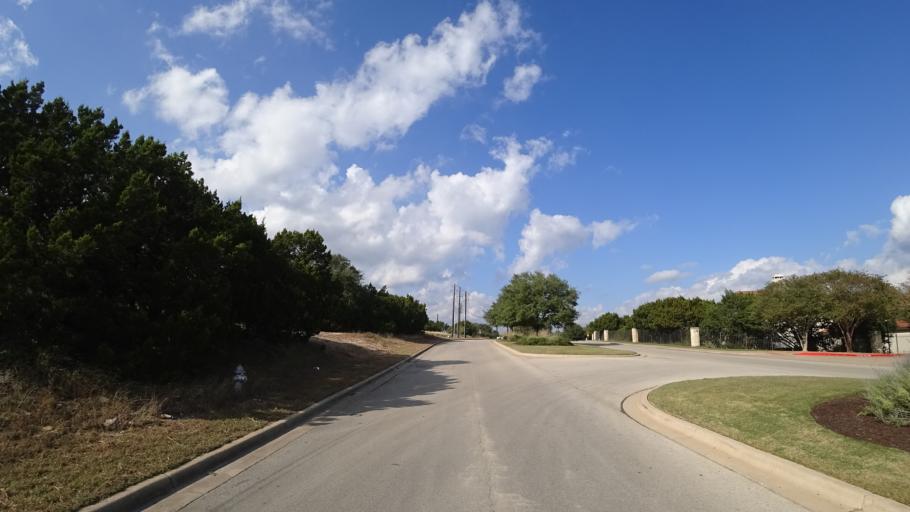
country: US
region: Texas
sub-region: Travis County
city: Barton Creek
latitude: 30.2900
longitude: -97.8730
